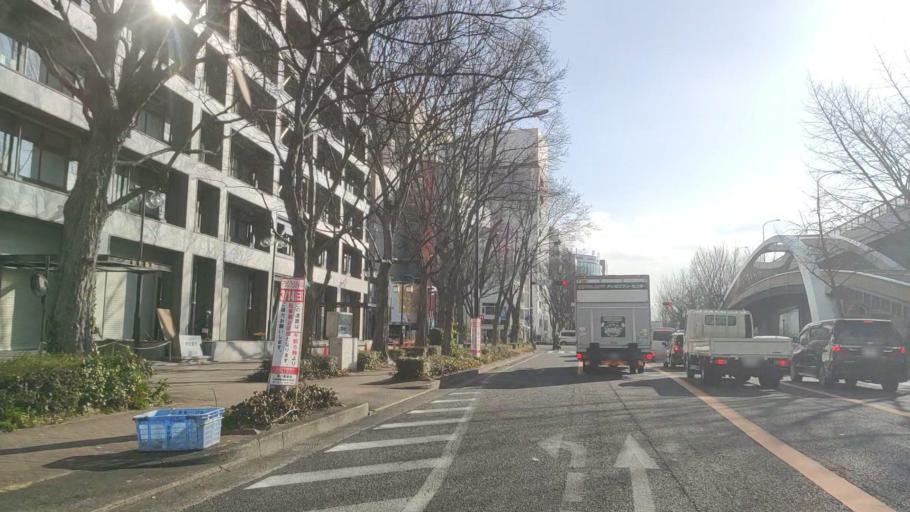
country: JP
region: Aichi
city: Nagoya-shi
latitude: 35.1627
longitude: 136.9058
